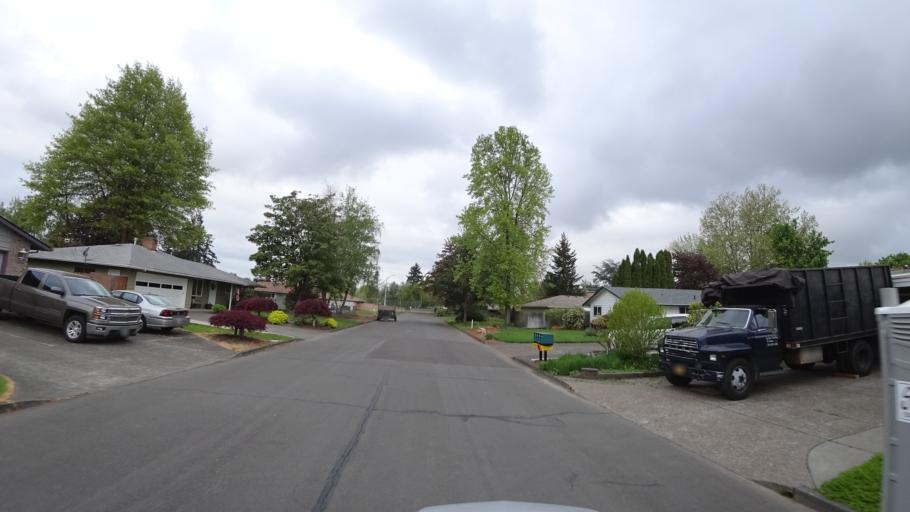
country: US
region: Oregon
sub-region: Washington County
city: Hillsboro
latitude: 45.5332
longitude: -122.9676
